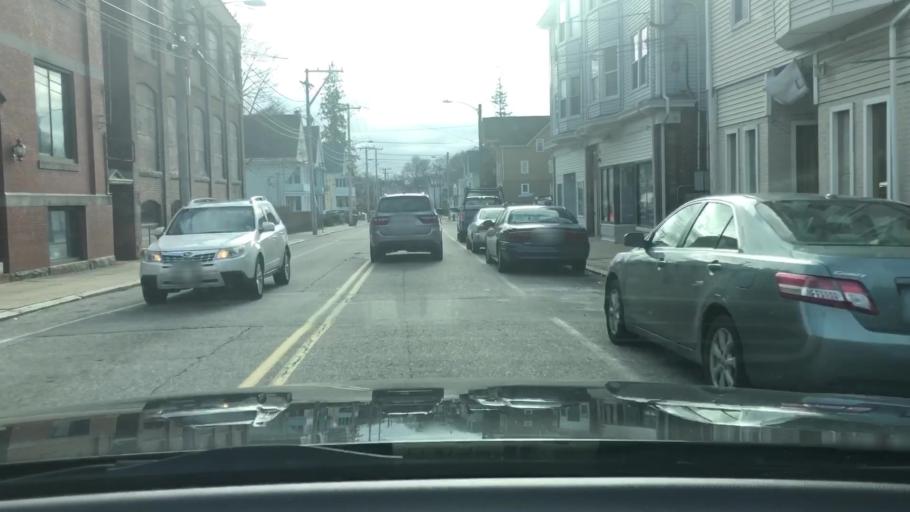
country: US
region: Rhode Island
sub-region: Providence County
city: Woonsocket
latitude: 42.0133
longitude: -71.5139
